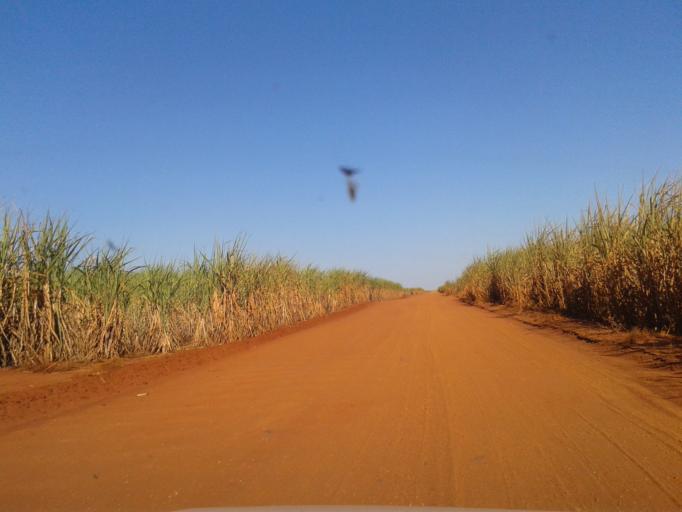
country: BR
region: Minas Gerais
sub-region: Santa Vitoria
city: Santa Vitoria
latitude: -18.8312
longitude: -50.0635
